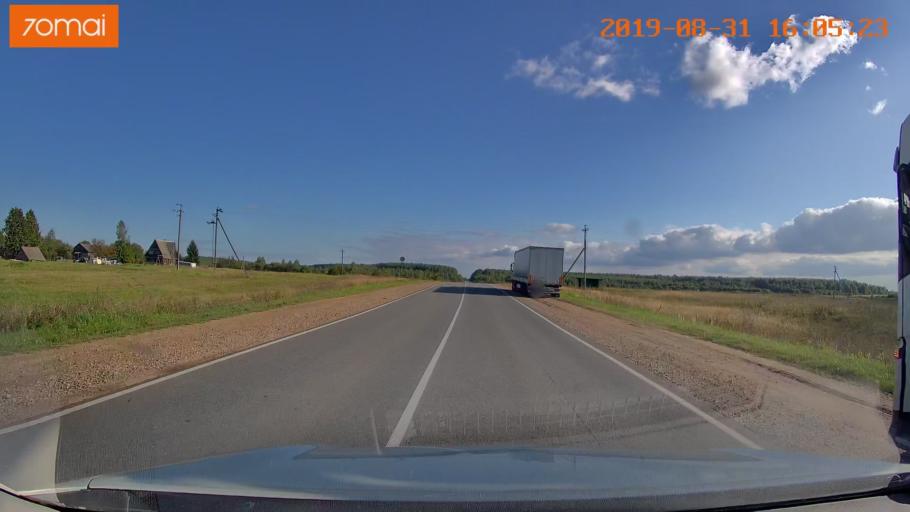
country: RU
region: Kaluga
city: Yukhnov
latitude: 54.6399
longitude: 35.3336
